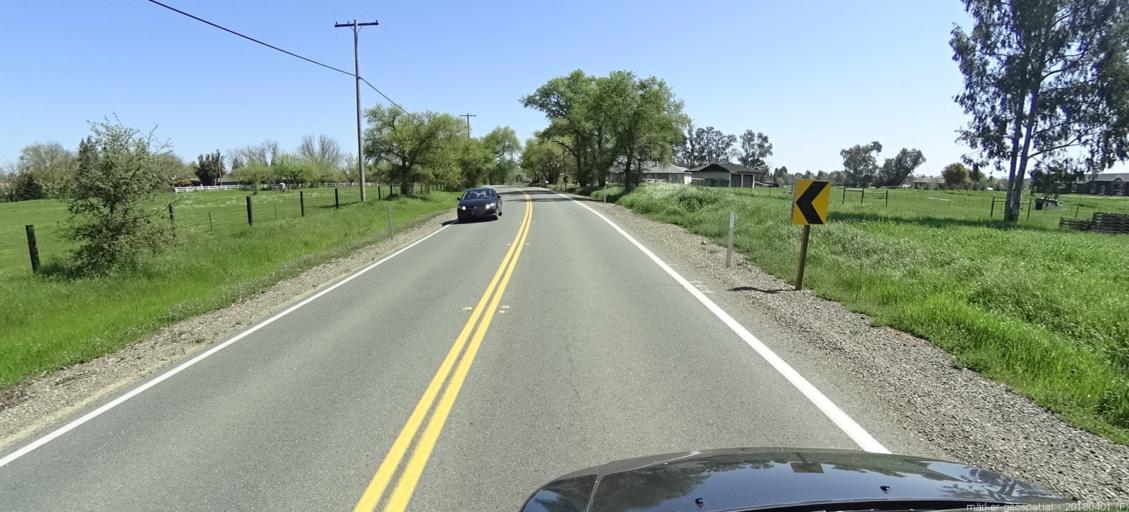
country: US
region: California
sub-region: Sacramento County
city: Wilton
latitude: 38.4119
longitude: -121.2610
